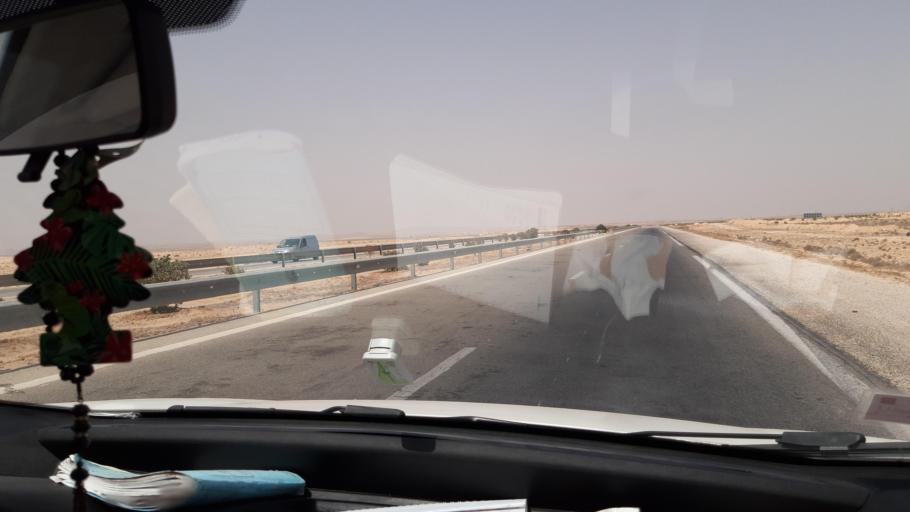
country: TN
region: Qabis
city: Gabes
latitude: 33.9486
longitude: 9.9595
